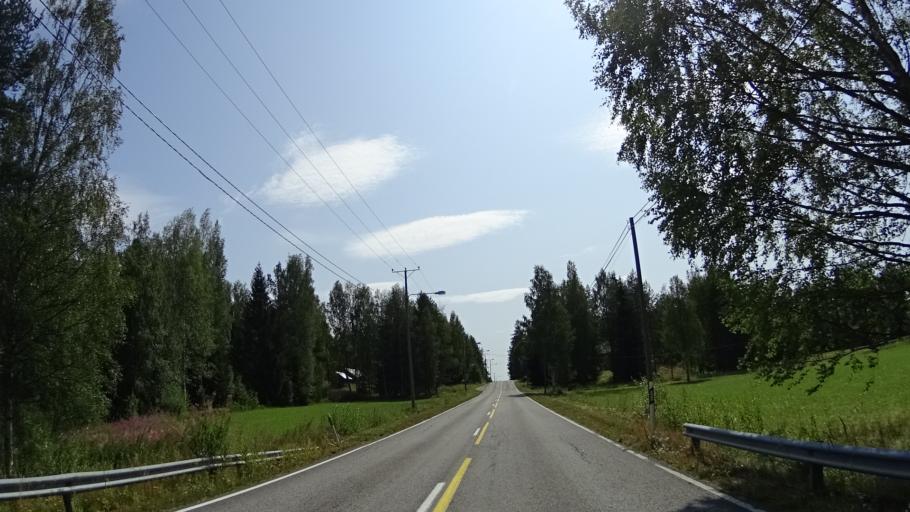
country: FI
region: Pirkanmaa
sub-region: Ylae-Pirkanmaa
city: Maenttae
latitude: 61.9034
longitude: 24.7896
